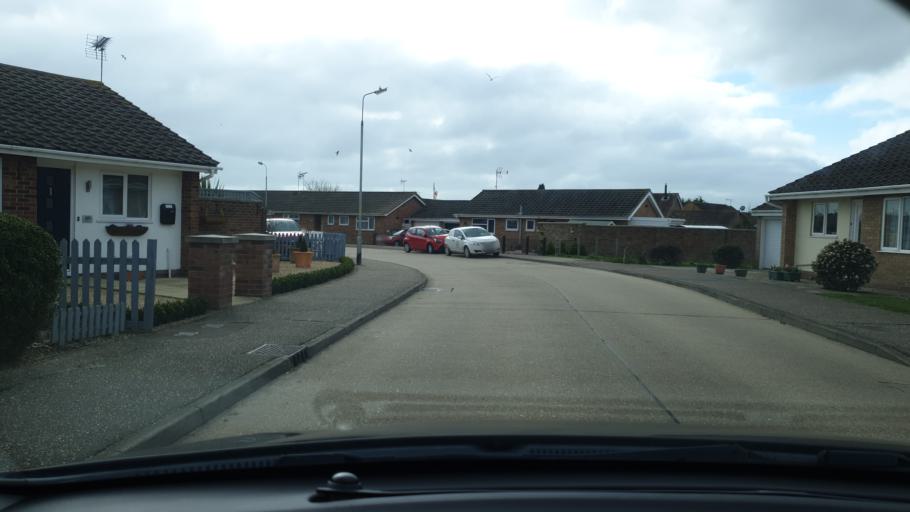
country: GB
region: England
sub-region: Essex
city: Little Clacton
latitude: 51.8141
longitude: 1.1551
